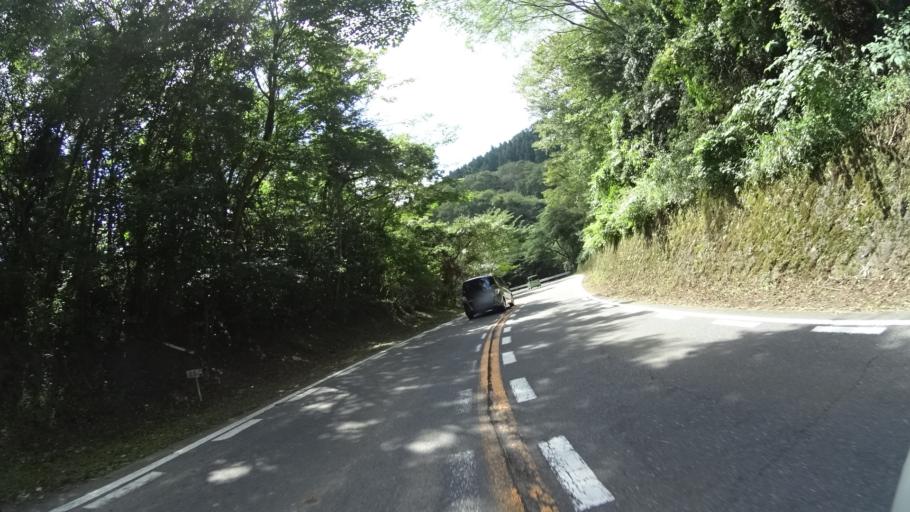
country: JP
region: Oita
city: Tsukawaki
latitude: 33.2328
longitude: 131.2942
